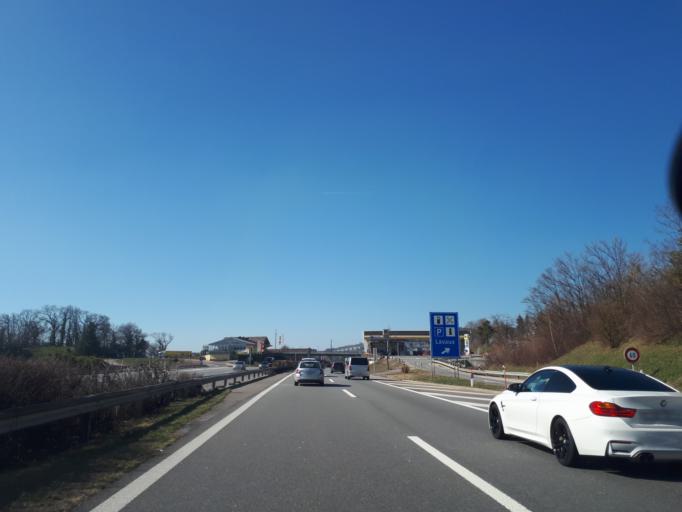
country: CH
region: Vaud
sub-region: Lavaux-Oron District
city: Cully
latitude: 46.5037
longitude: 6.7123
